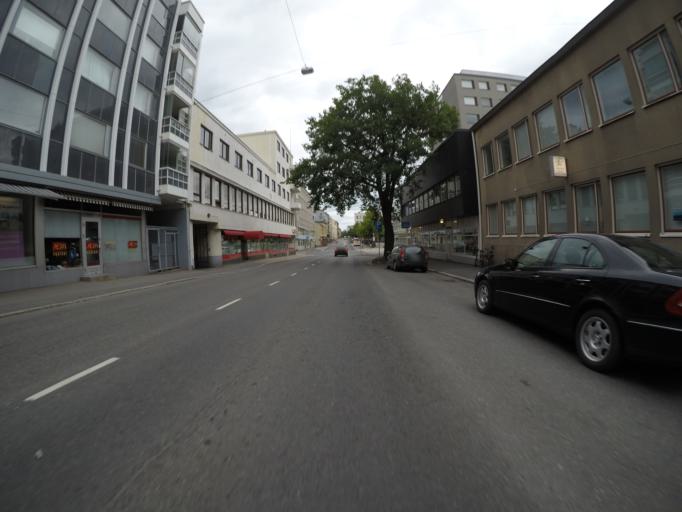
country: FI
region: Haeme
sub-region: Haemeenlinna
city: Haemeenlinna
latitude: 60.9948
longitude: 24.4640
